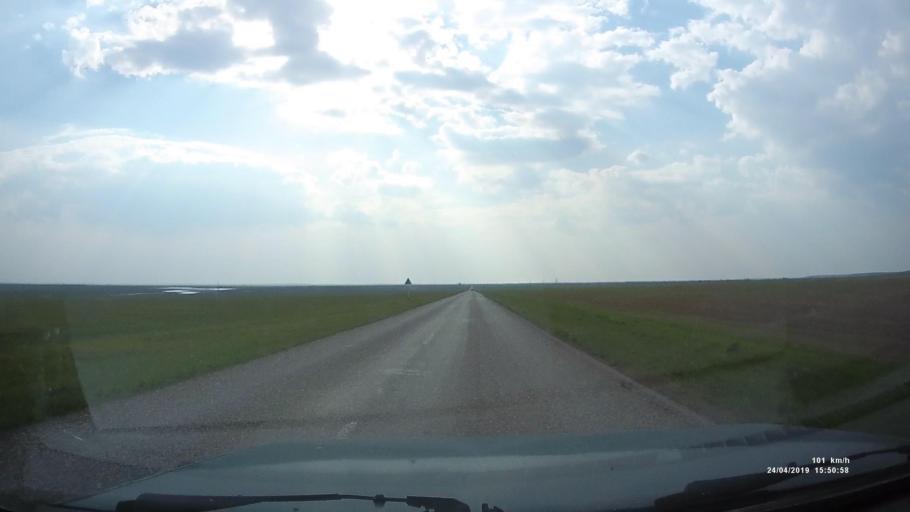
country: RU
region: Kalmykiya
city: Yashalta
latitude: 46.6042
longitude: 42.6216
